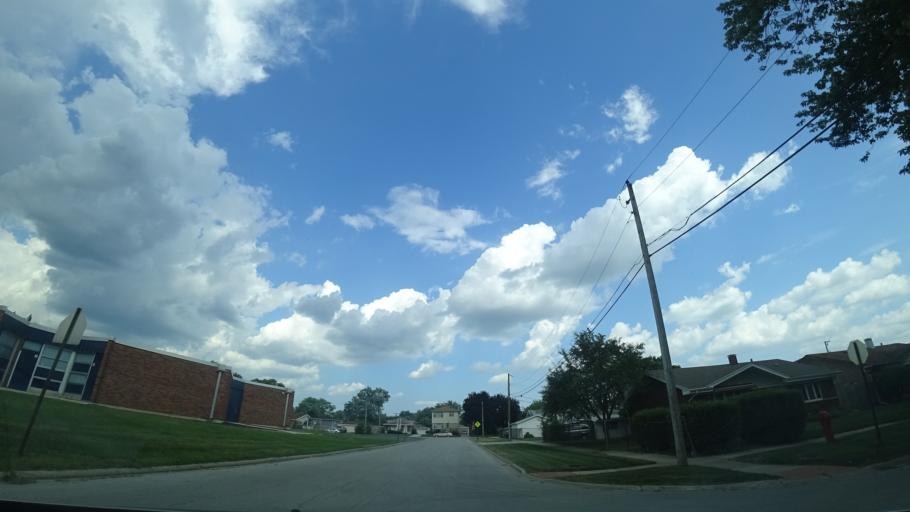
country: US
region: Illinois
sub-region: Cook County
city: Merrionette Park
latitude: 41.6712
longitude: -87.7160
